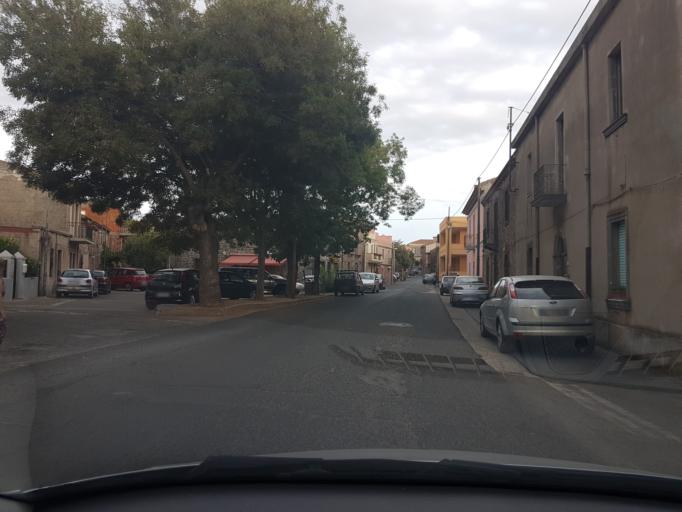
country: IT
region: Sardinia
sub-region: Provincia di Oristano
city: Seneghe
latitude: 40.0820
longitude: 8.6094
